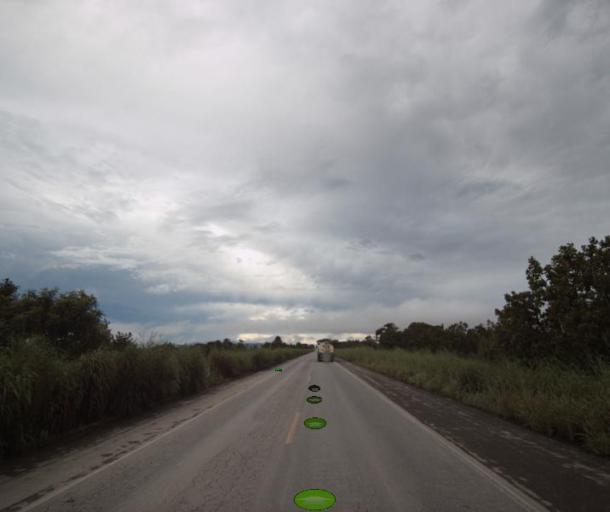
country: BR
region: Goias
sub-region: Porangatu
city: Porangatu
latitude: -13.5214
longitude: -49.1171
